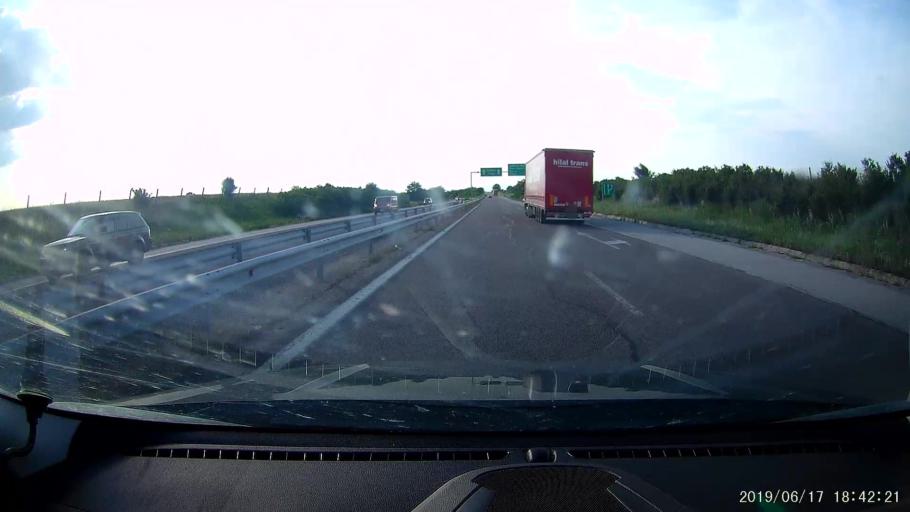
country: BG
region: Stara Zagora
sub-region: Obshtina Chirpan
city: Chirpan
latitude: 42.1898
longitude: 25.2386
